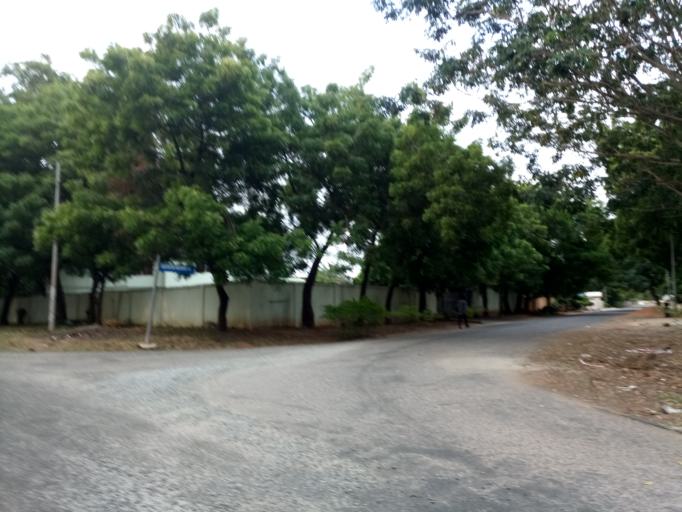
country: GH
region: Greater Accra
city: Accra
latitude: 5.5618
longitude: -0.1903
